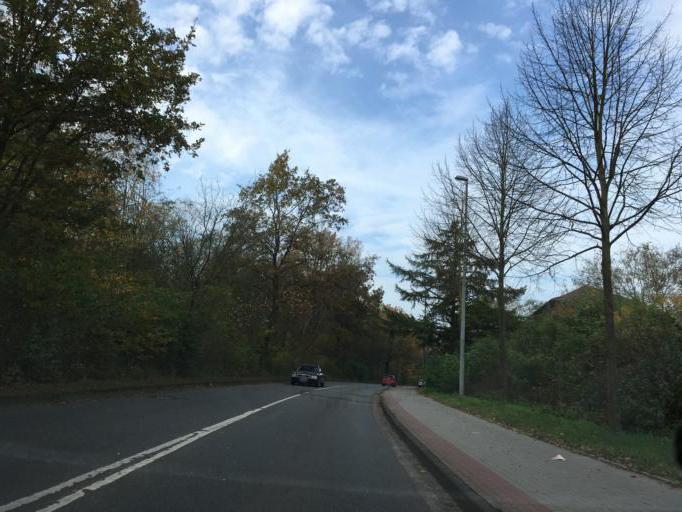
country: DE
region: Lower Saxony
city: Wendisch Evern
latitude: 53.2316
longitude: 10.4447
